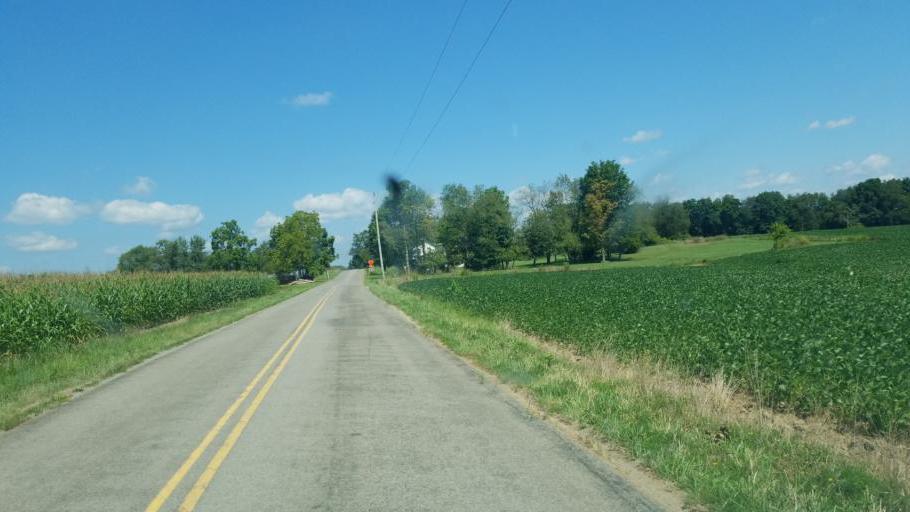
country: US
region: Pennsylvania
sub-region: Clarion County
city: Knox
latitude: 41.1950
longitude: -79.4920
